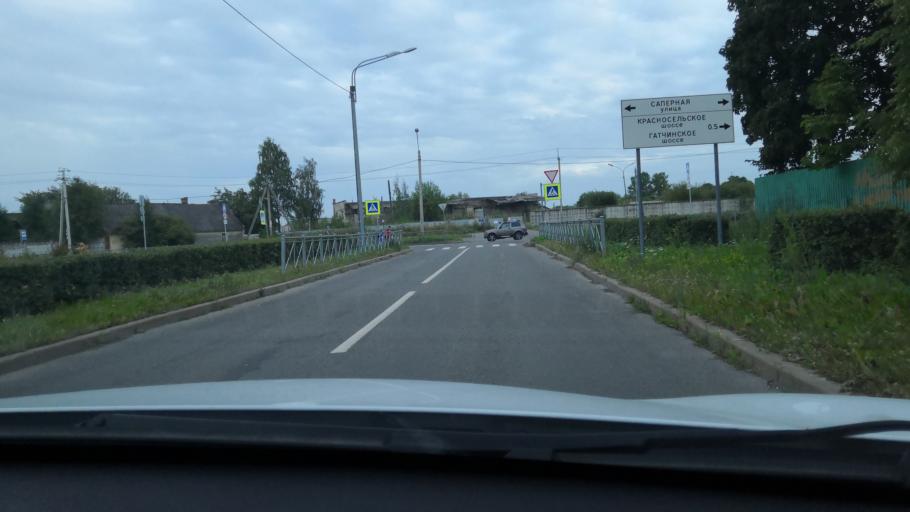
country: RU
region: St.-Petersburg
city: Pushkin
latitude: 59.7010
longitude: 30.3885
